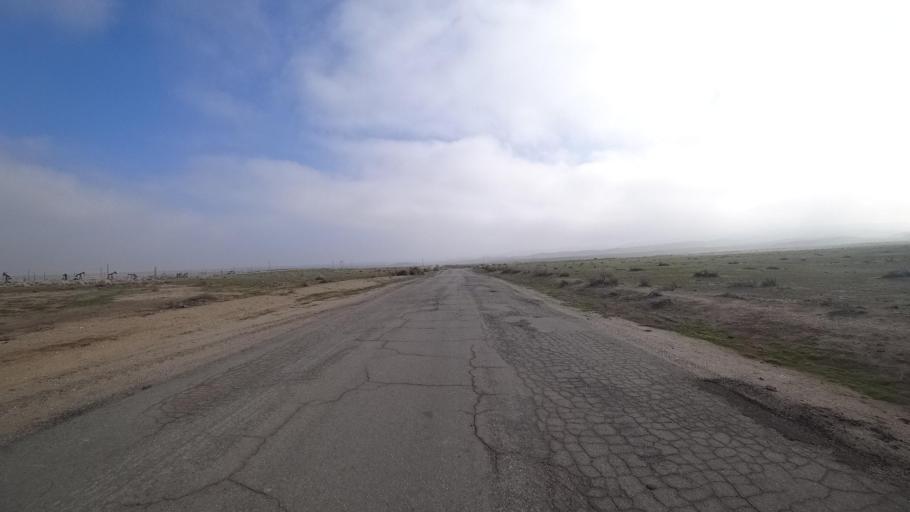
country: US
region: California
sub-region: Kern County
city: Maricopa
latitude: 35.0286
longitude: -119.3409
